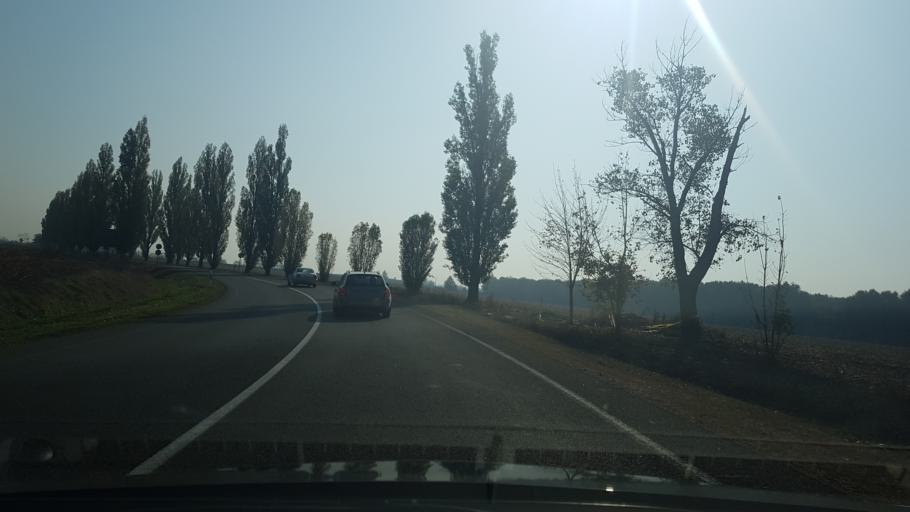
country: HU
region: Fejer
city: Ivancsa
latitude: 47.1297
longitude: 18.8221
